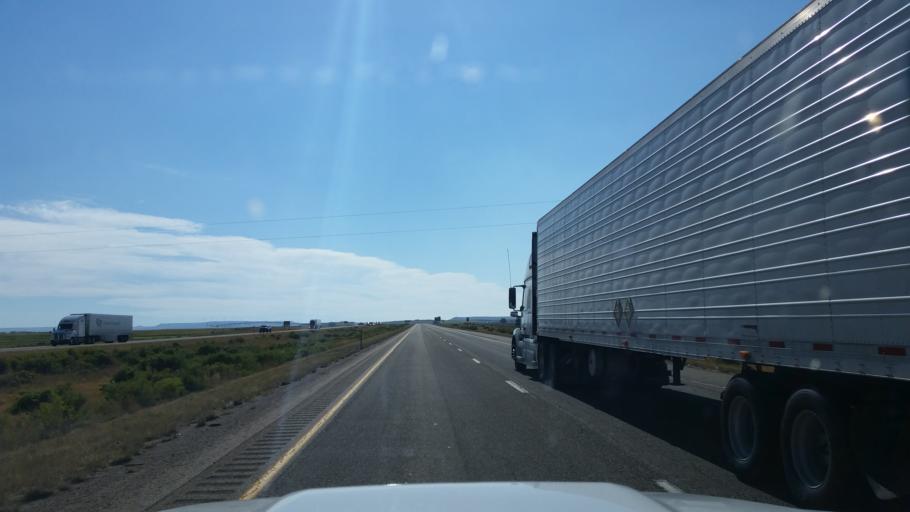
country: US
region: Wyoming
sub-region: Uinta County
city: Lyman
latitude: 41.3656
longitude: -110.3068
